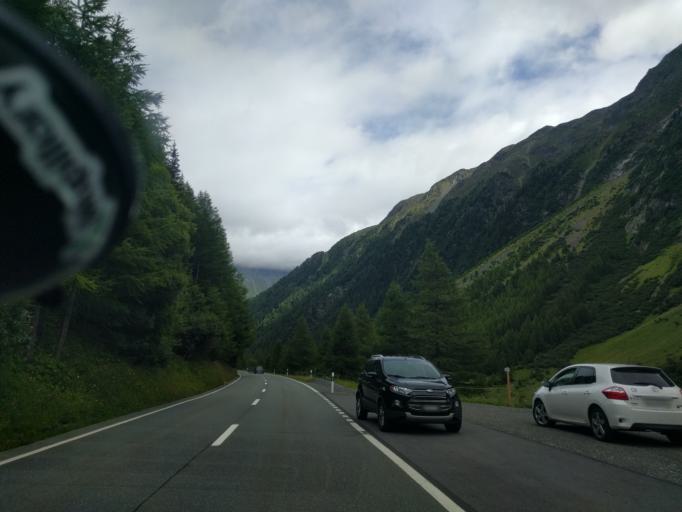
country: CH
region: Grisons
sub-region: Inn District
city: Zernez
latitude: 46.7533
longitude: 10.0362
